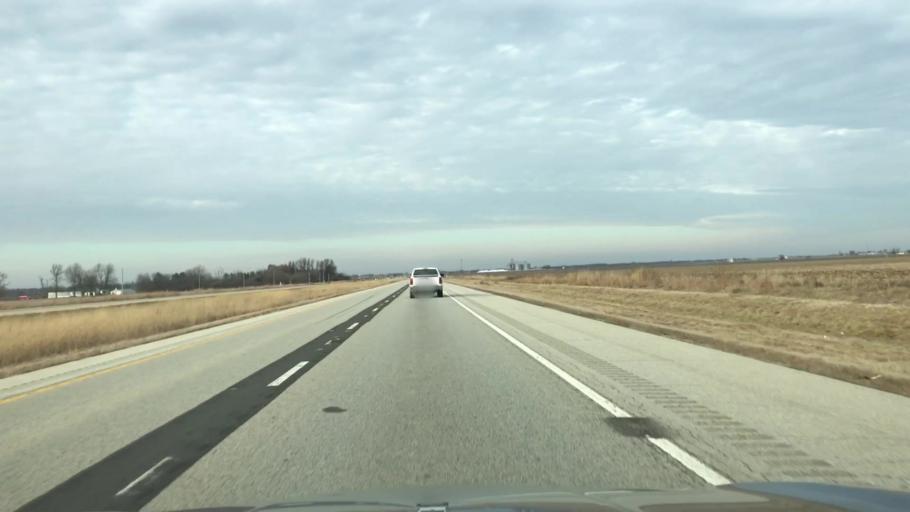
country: US
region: Illinois
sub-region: Sangamon County
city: Divernon
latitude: 39.5344
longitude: -89.6455
